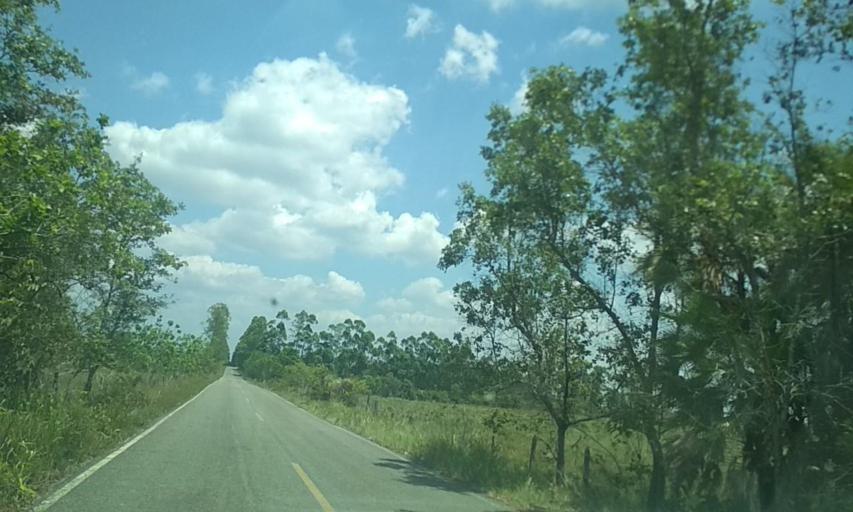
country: MX
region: Tabasco
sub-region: Huimanguillo
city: Francisco Rueda
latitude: 17.7666
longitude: -93.7972
